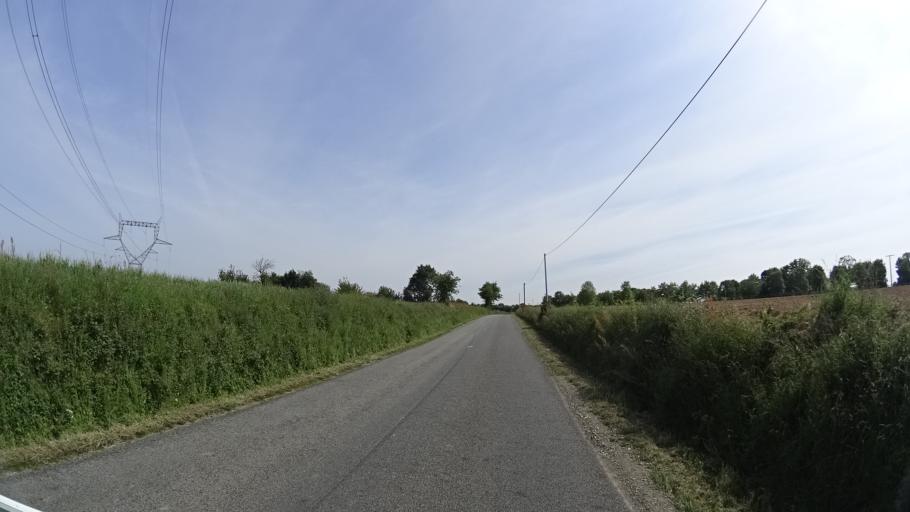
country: FR
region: Brittany
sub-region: Departement d'Ille-et-Vilaine
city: Nouvoitou
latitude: 48.0300
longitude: -1.5322
